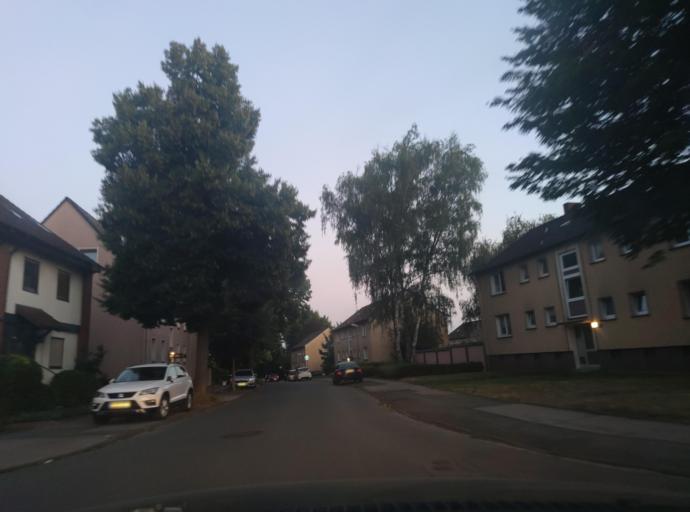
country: DE
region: North Rhine-Westphalia
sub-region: Regierungsbezirk Dusseldorf
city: Essen
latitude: 51.4719
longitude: 7.0620
